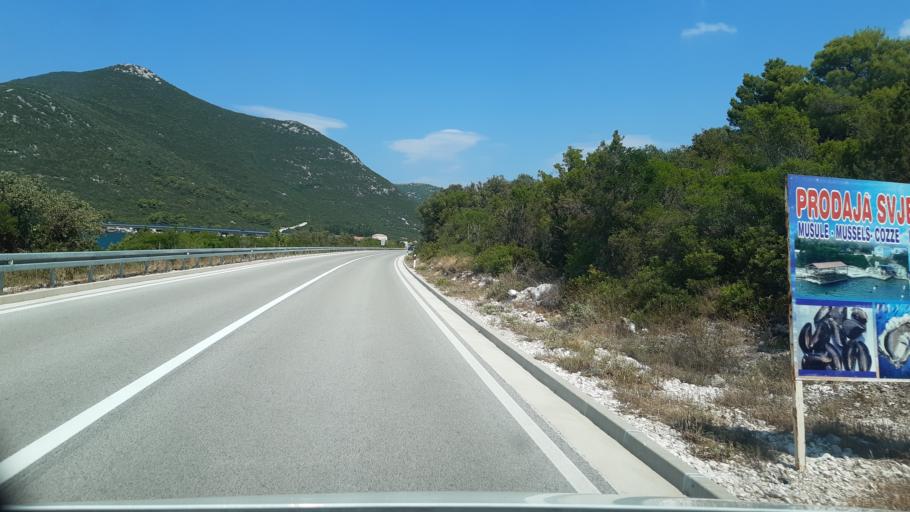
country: HR
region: Dubrovacko-Neretvanska
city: Ston
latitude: 42.8632
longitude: 17.7031
